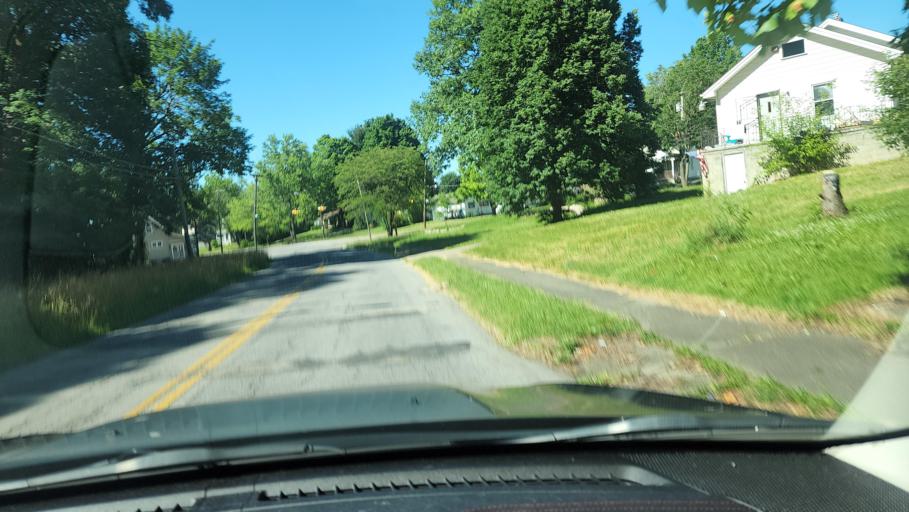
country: US
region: Ohio
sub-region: Mahoning County
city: Struthers
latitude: 41.0637
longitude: -80.6198
